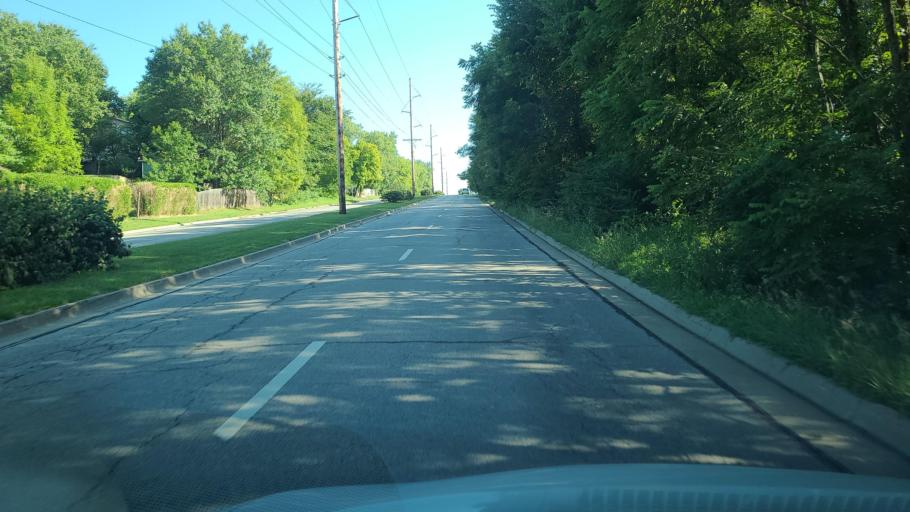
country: US
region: Kansas
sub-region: Douglas County
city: Lawrence
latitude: 38.9807
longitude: -95.2792
